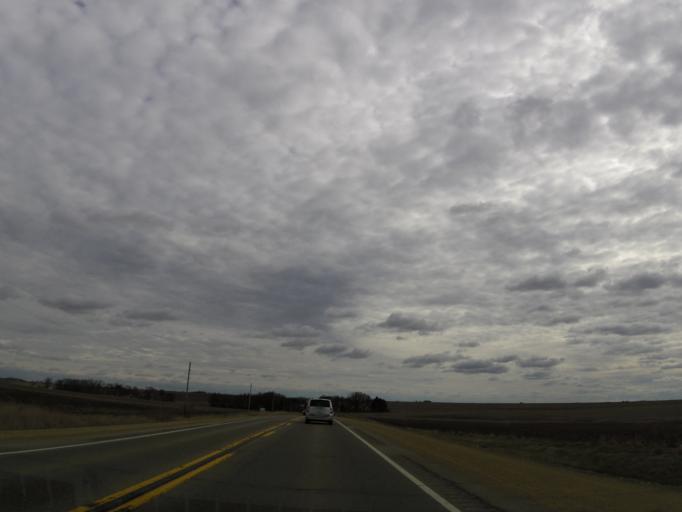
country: US
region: Iowa
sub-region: Chickasaw County
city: New Hampton
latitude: 43.1764
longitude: -92.2986
